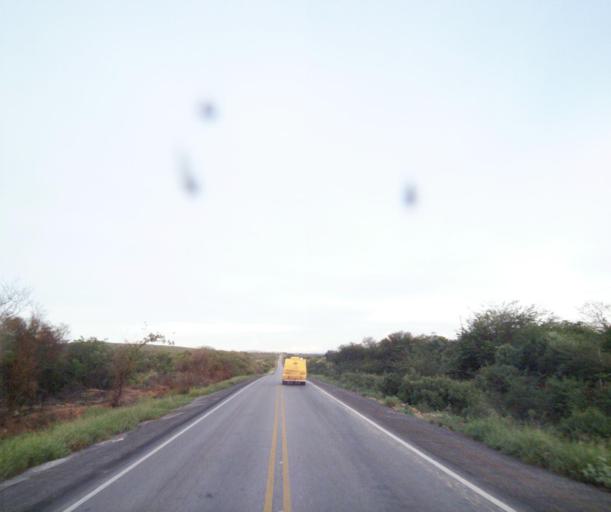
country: BR
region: Bahia
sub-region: Brumado
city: Brumado
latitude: -14.2554
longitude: -41.7599
